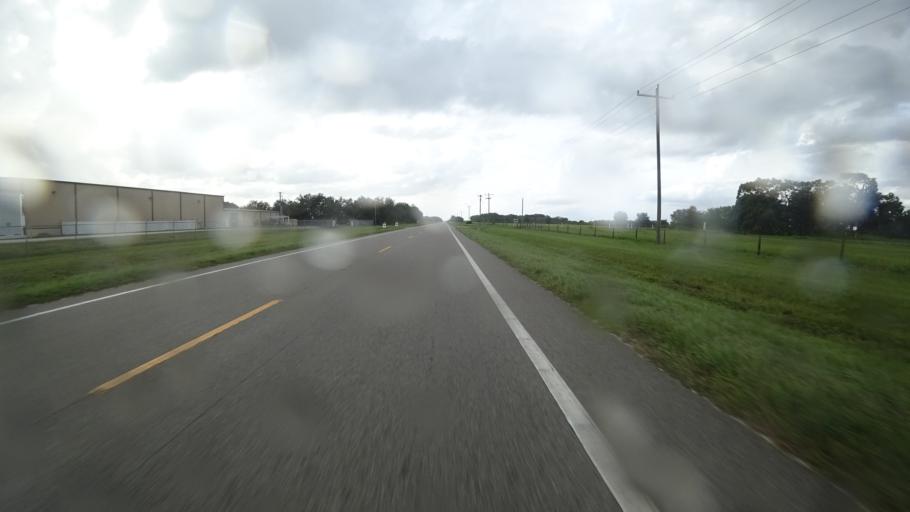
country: US
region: Florida
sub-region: Hillsborough County
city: Wimauma
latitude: 27.5957
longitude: -82.2749
